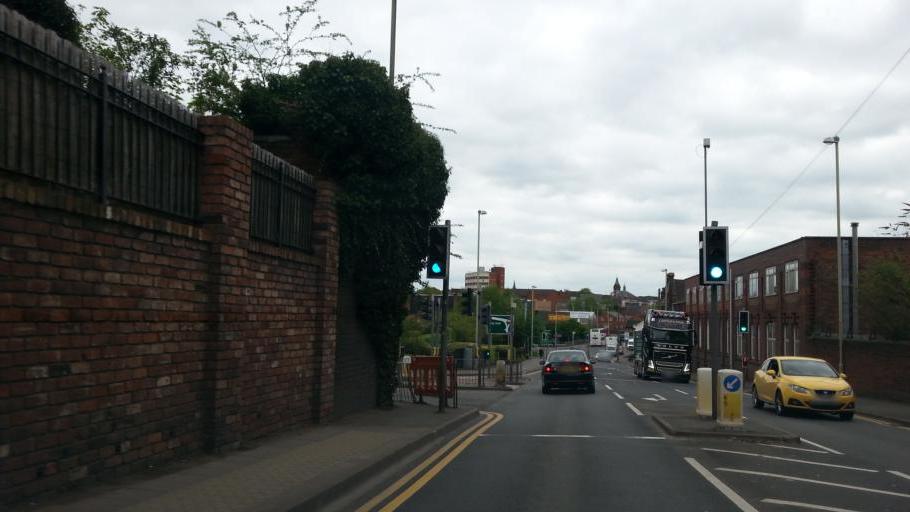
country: GB
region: England
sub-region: Dudley
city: Stourbridge
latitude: 52.4625
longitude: -2.1494
